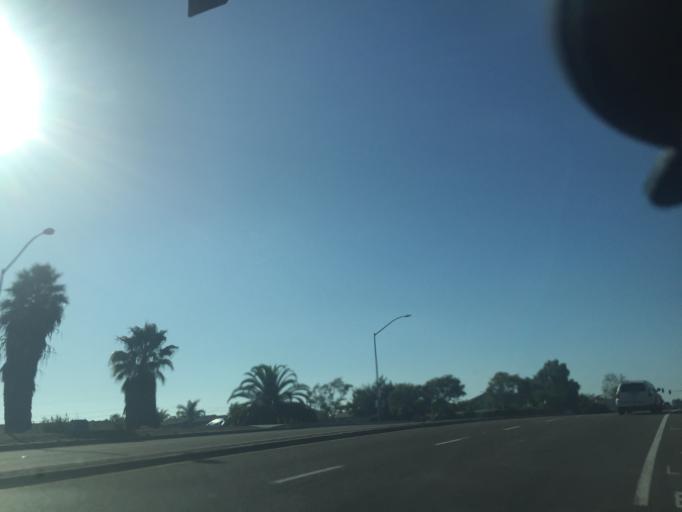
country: US
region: California
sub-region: San Diego County
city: San Diego
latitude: 32.7913
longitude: -117.1607
